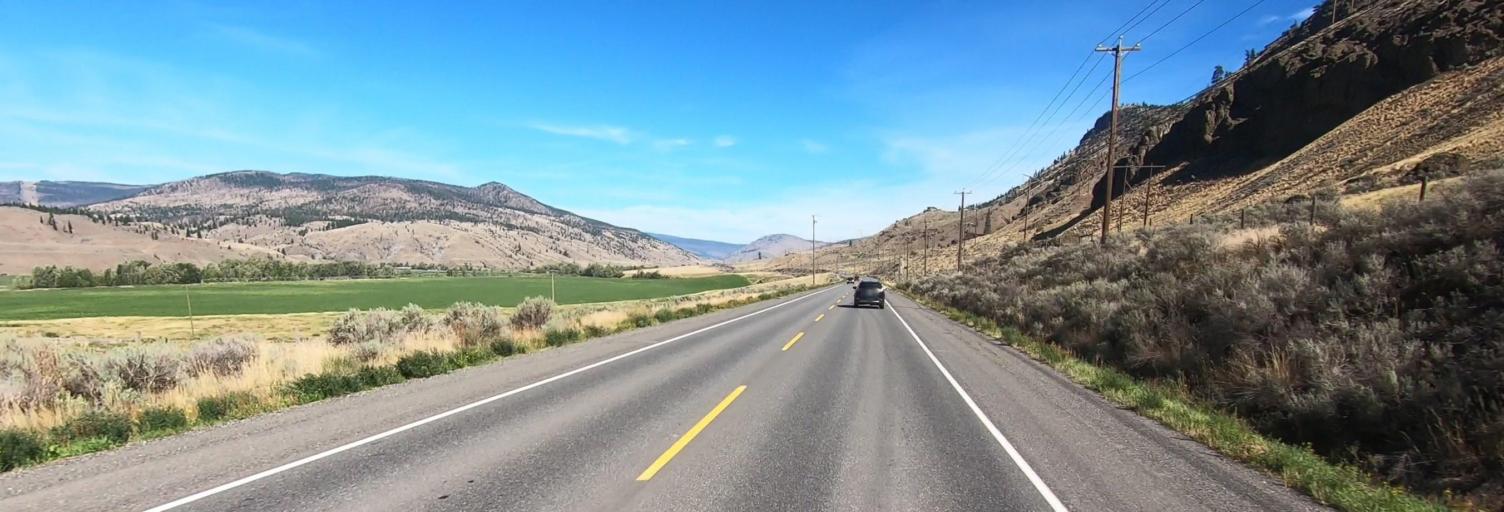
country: CA
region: British Columbia
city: Cache Creek
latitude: 50.8715
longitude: -121.3918
